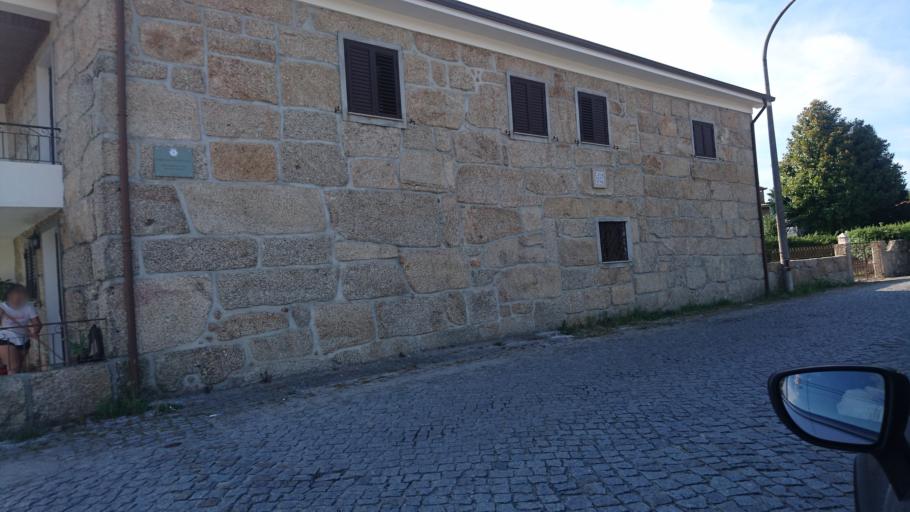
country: PT
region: Porto
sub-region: Paredes
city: Recarei
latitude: 41.1275
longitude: -8.3689
